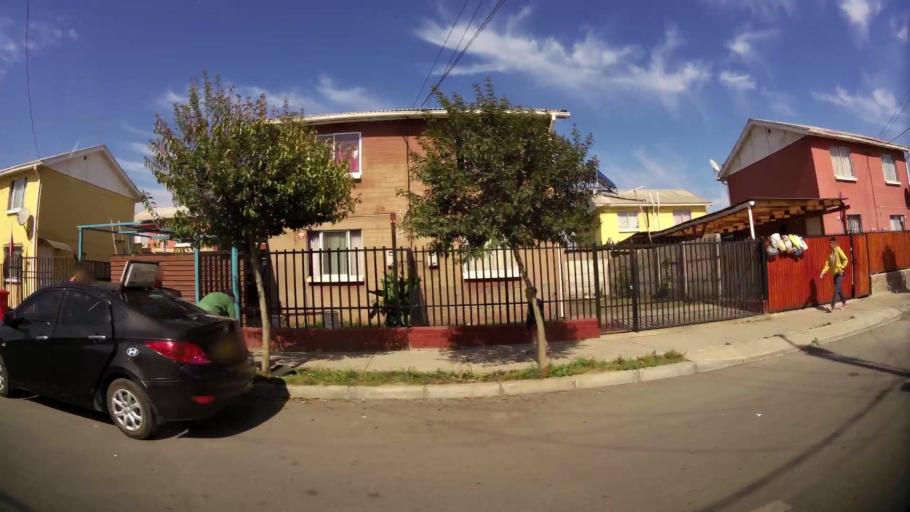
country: CL
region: Santiago Metropolitan
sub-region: Provincia de Talagante
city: El Monte
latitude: -33.6833
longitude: -70.9540
